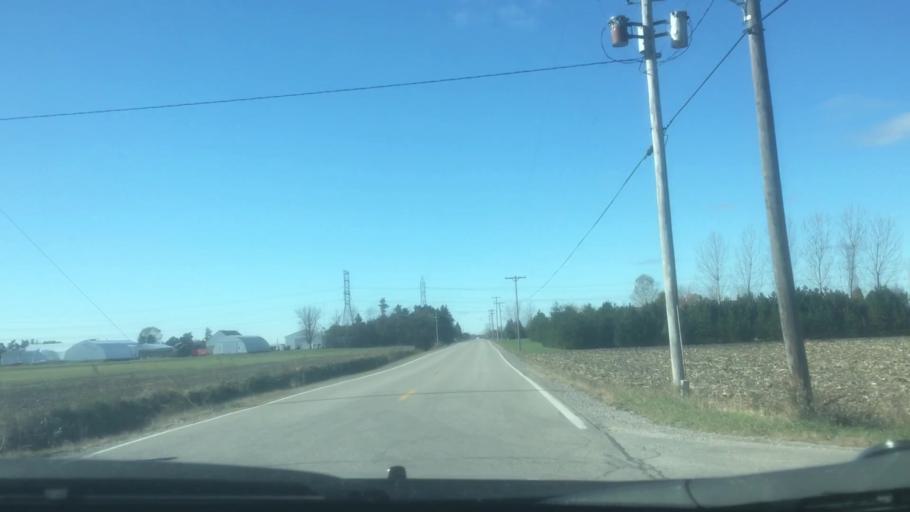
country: US
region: Michigan
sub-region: Bay County
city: Essexville
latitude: 43.5799
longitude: -83.7896
